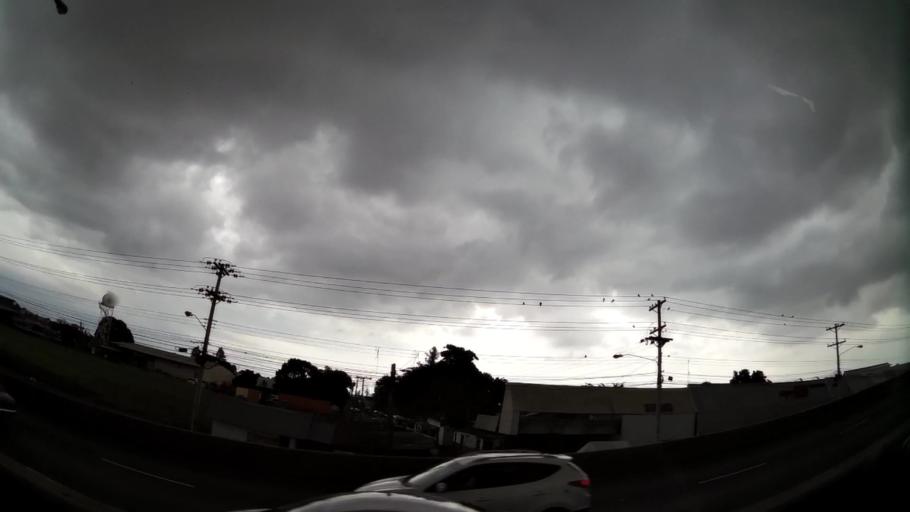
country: PA
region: Panama
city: San Miguelito
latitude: 9.0585
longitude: -79.4319
